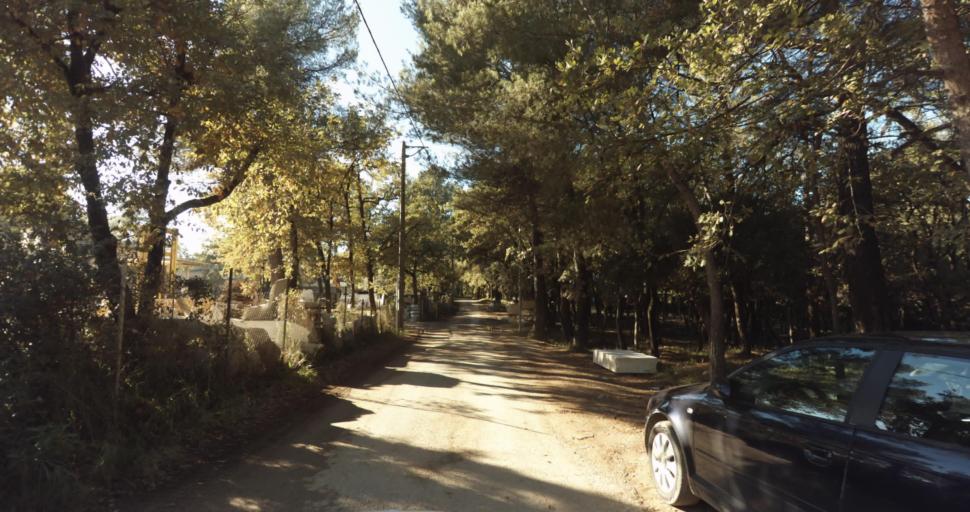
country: FR
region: Provence-Alpes-Cote d'Azur
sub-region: Departement des Alpes-Maritimes
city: Vence
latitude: 43.7113
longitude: 7.0857
